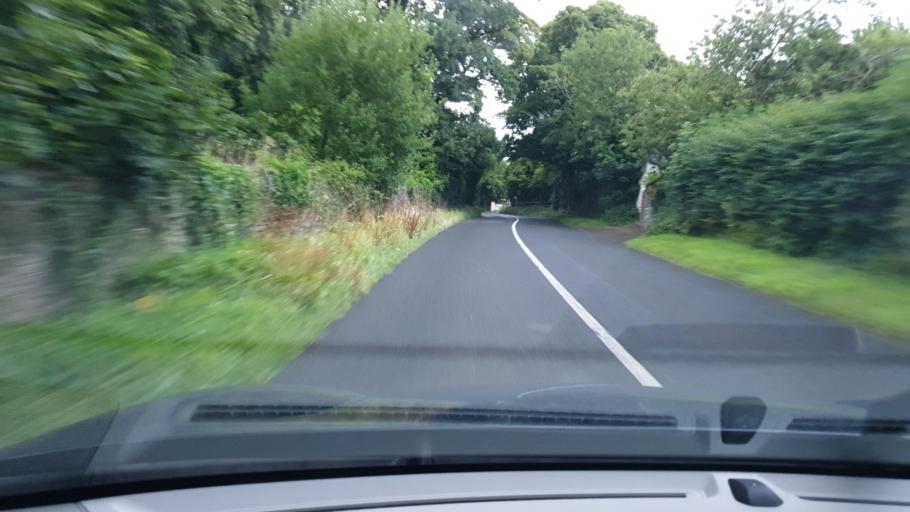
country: IE
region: Leinster
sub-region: South Dublin
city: Rathcoole
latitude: 53.2596
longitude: -6.4967
